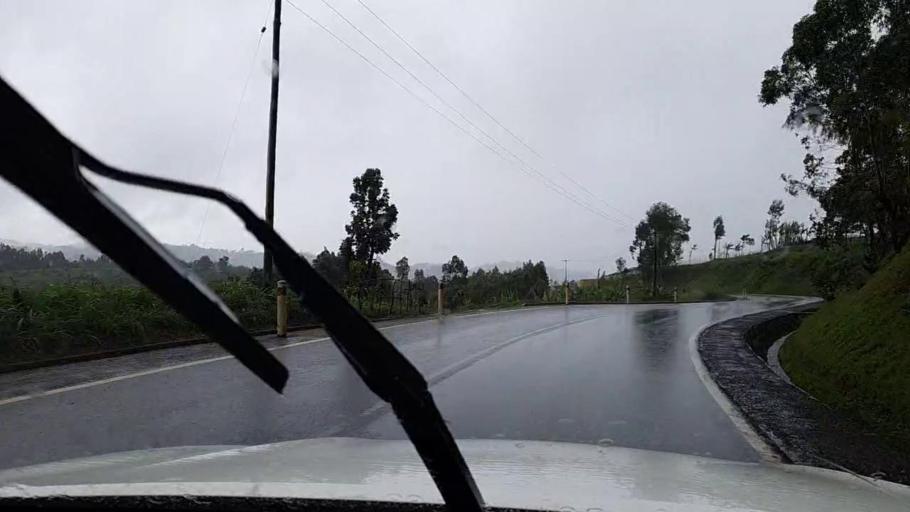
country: RW
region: Western Province
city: Cyangugu
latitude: -2.4622
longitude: 28.9913
